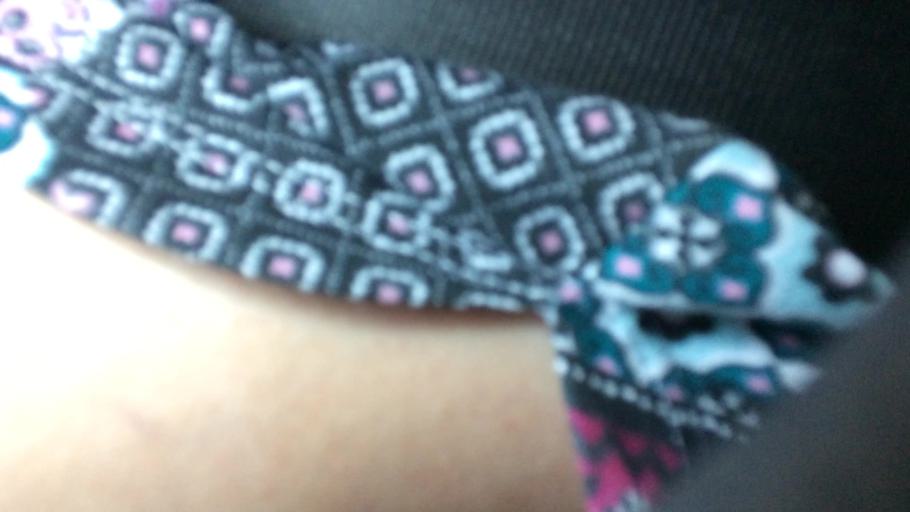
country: US
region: New Mexico
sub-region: Colfax County
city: Springer
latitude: 36.2289
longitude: -104.6552
